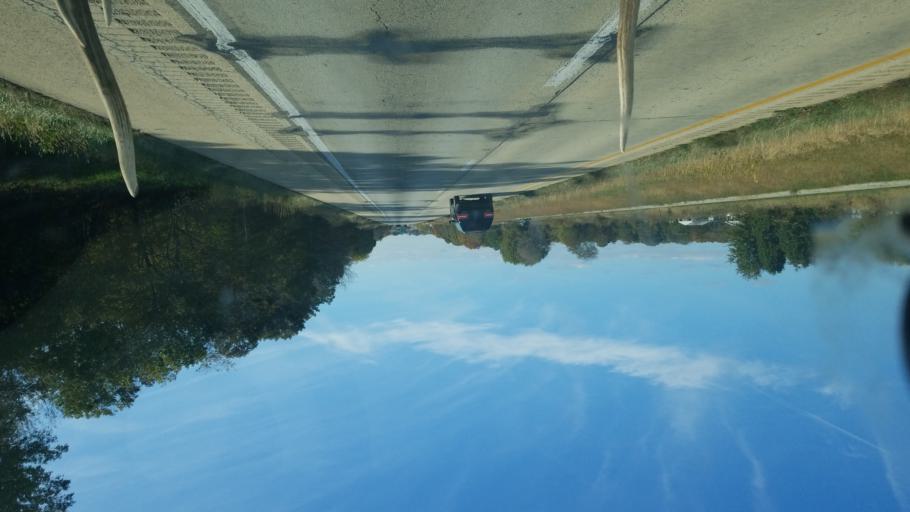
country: US
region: Illinois
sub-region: Effingham County
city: Effingham
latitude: 39.0857
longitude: -88.6107
